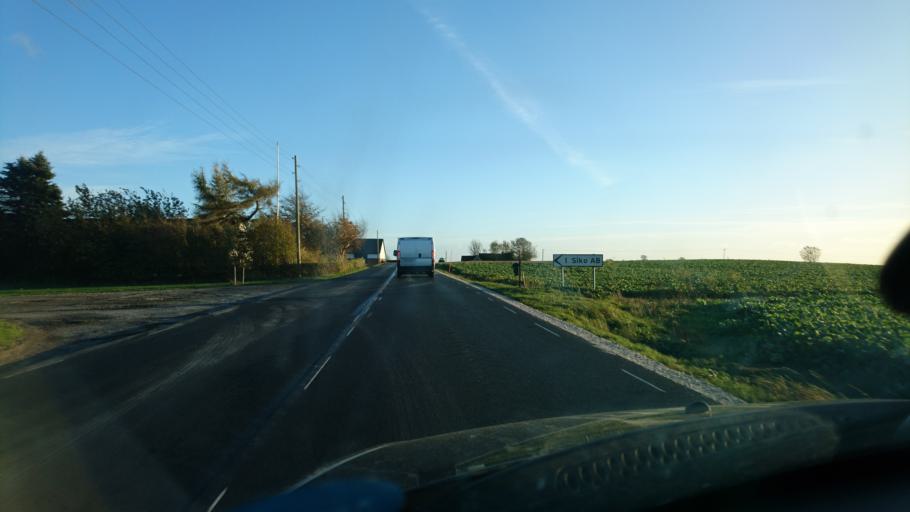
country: SE
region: Skane
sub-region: Tomelilla Kommun
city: Tomelilla
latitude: 55.5298
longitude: 14.1252
